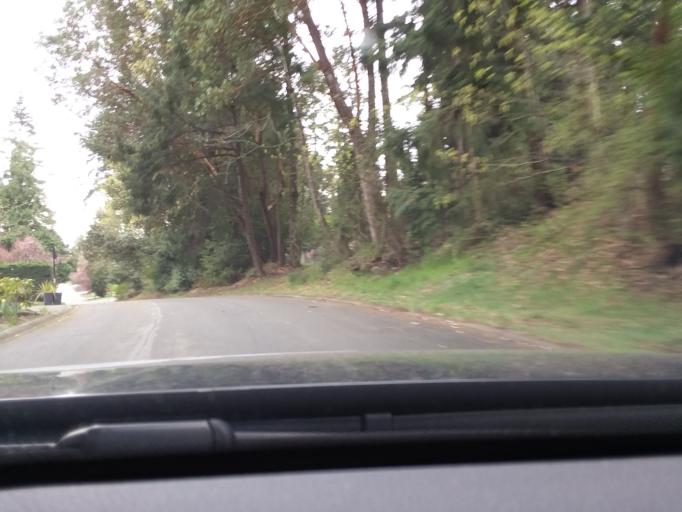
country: CA
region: British Columbia
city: North Saanich
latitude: 48.6185
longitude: -123.4232
